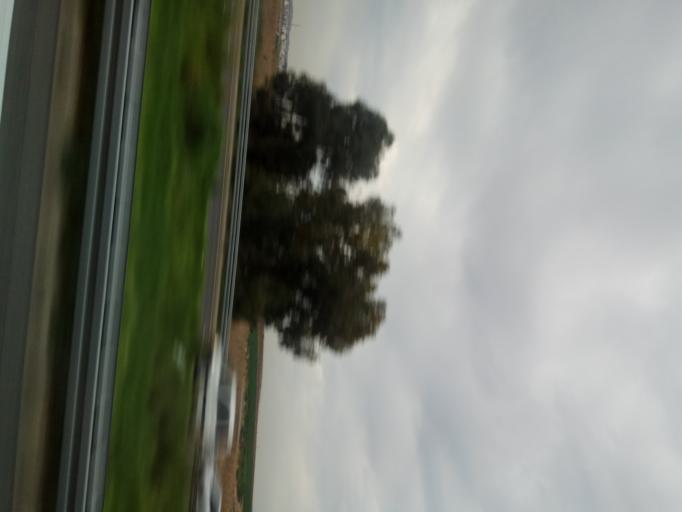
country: IL
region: Central District
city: Mazkeret Batya
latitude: 31.8432
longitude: 34.8639
